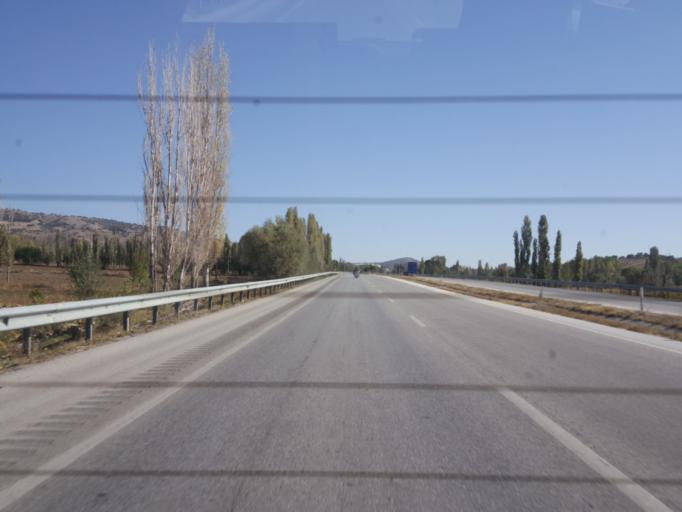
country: TR
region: Corum
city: Bogazkale
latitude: 40.2409
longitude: 34.5891
